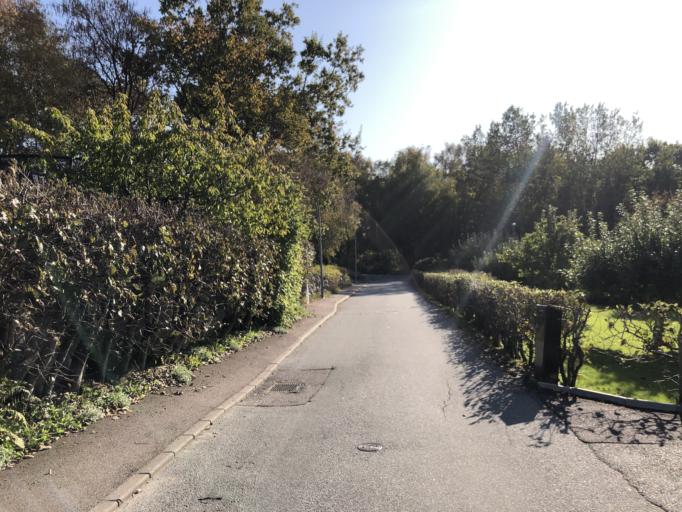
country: SE
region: Vaestra Goetaland
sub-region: Goteborg
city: Billdal
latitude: 57.6209
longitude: 11.8853
